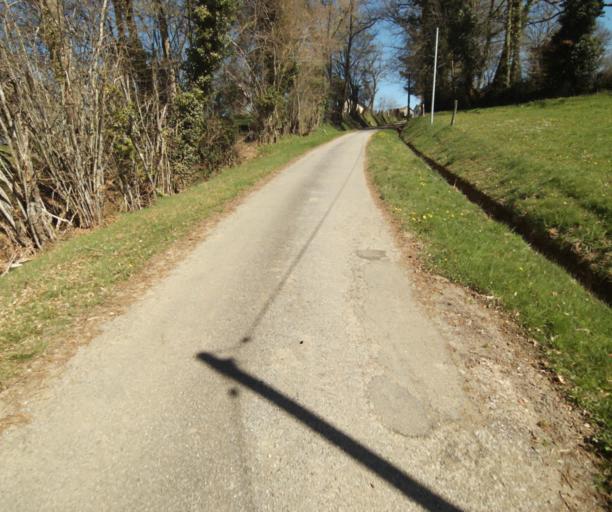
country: FR
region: Limousin
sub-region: Departement de la Correze
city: Chamboulive
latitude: 45.4021
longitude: 1.6747
